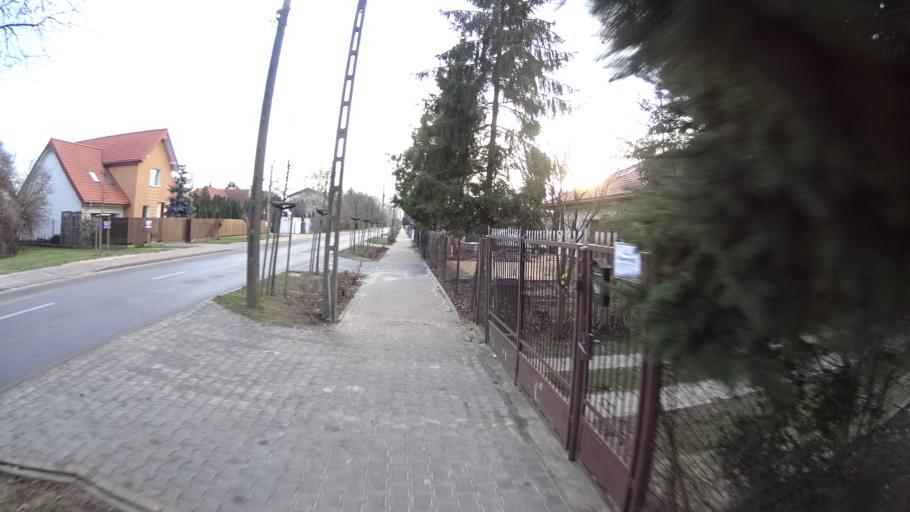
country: PL
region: Masovian Voivodeship
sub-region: Powiat warszawski zachodni
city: Ozarow Mazowiecki
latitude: 52.2247
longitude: 20.8014
